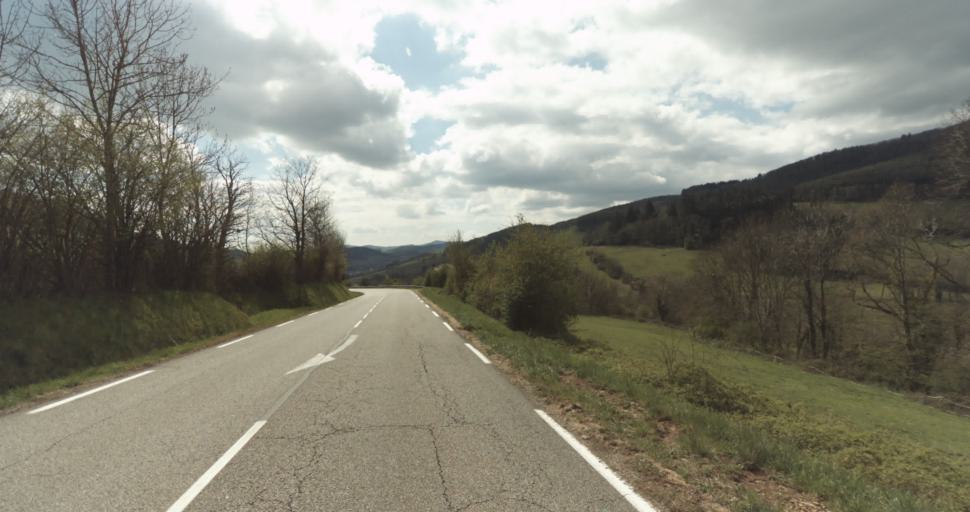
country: FR
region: Rhone-Alpes
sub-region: Departement du Rhone
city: Tarare
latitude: 45.9204
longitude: 4.4126
